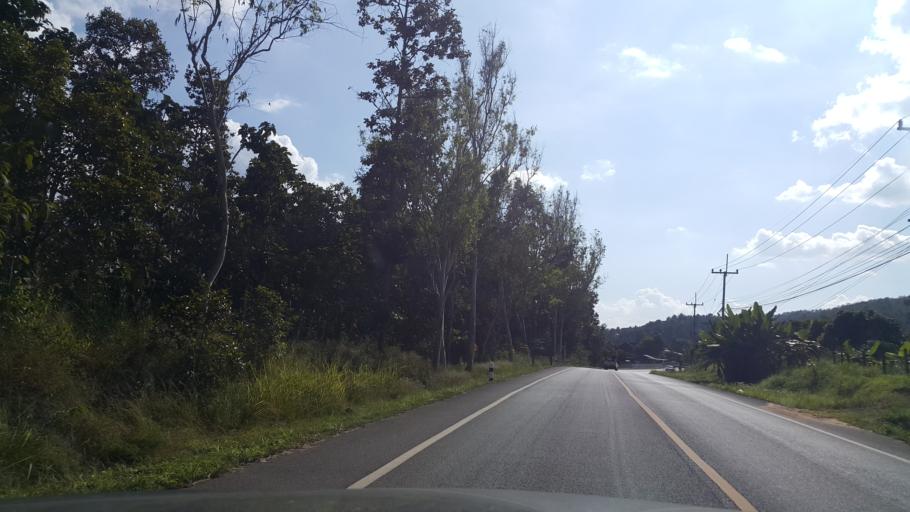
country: TH
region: Lamphun
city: Mae Tha
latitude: 18.5407
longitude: 99.2378
